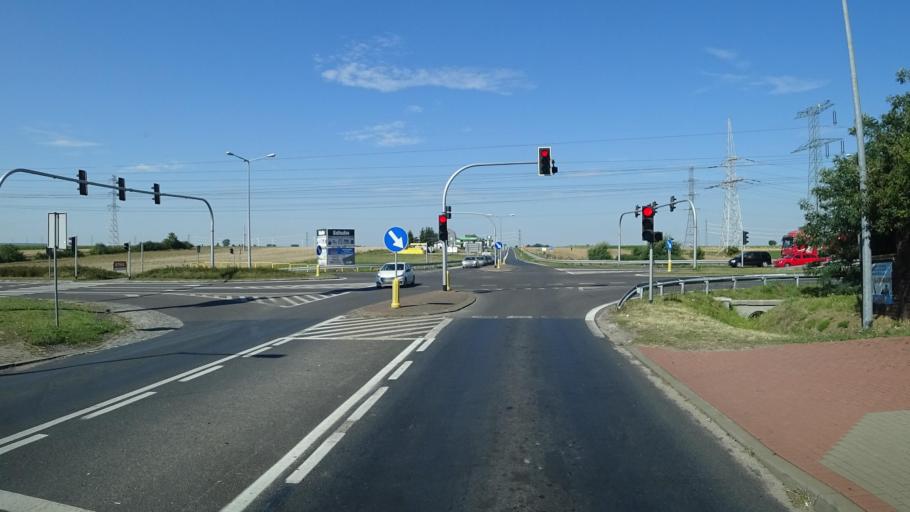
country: PL
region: Greater Poland Voivodeship
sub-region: Powiat koninski
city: Slesin
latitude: 52.3714
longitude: 18.2970
